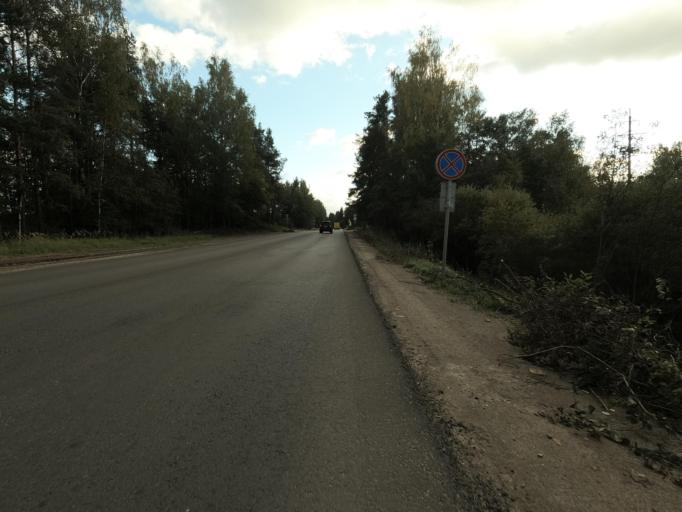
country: RU
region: Leningrad
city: Koltushi
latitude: 59.9641
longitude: 30.6584
